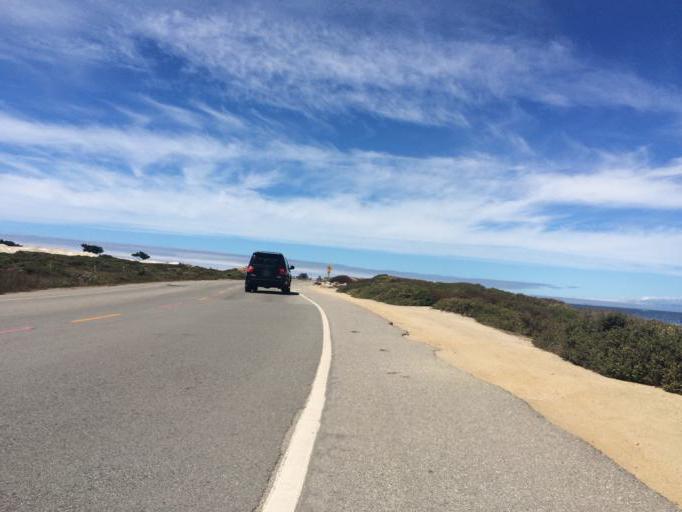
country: US
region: California
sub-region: Monterey County
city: Del Monte Forest
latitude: 36.6087
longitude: -121.9543
